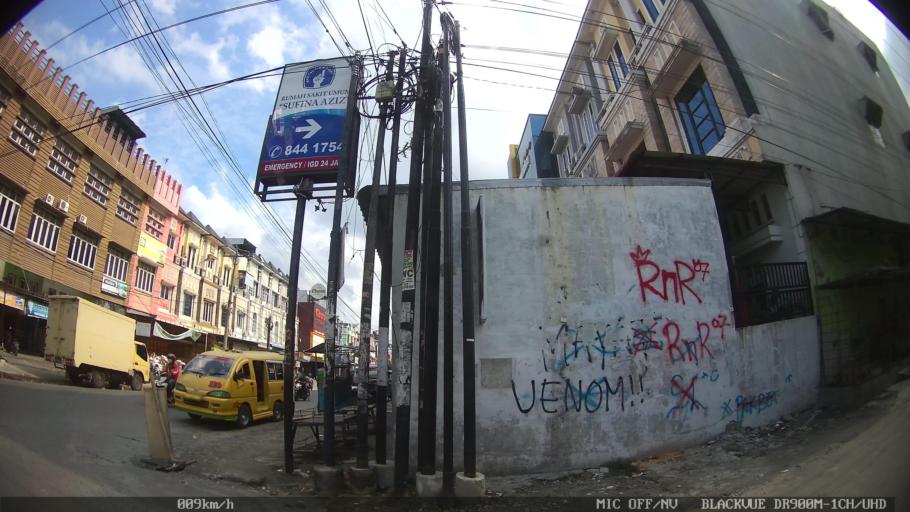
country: ID
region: North Sumatra
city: Medan
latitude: 3.6169
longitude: 98.6658
